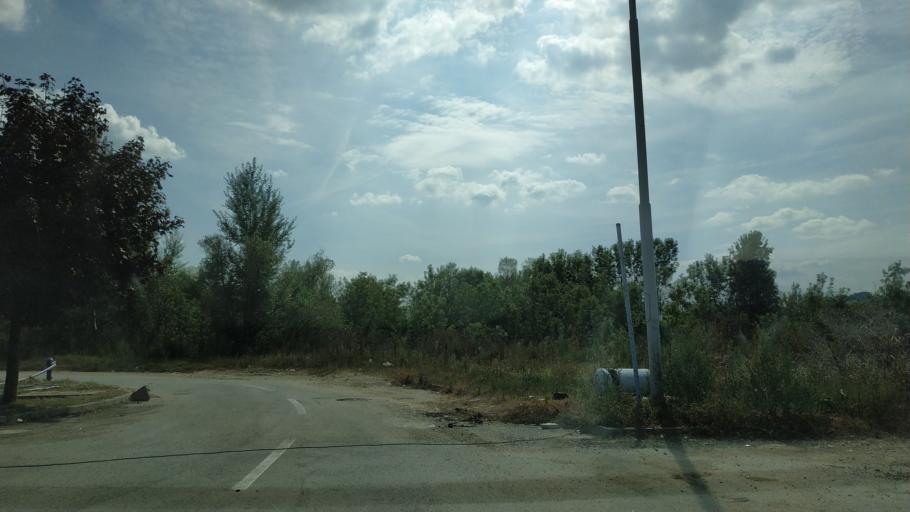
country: RS
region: Central Serbia
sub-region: Belgrade
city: Zvezdara
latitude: 44.6930
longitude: 20.5826
